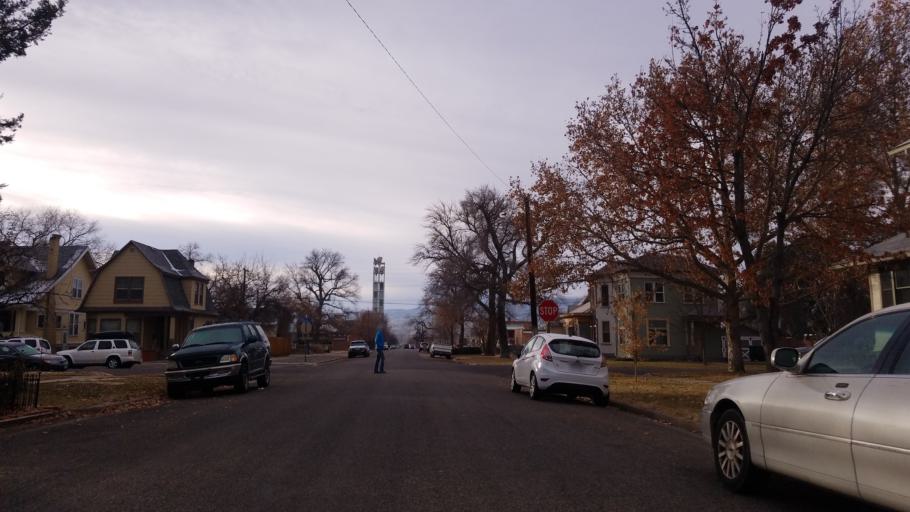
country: US
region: Colorado
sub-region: Mesa County
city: Grand Junction
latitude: 39.0717
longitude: -108.5594
